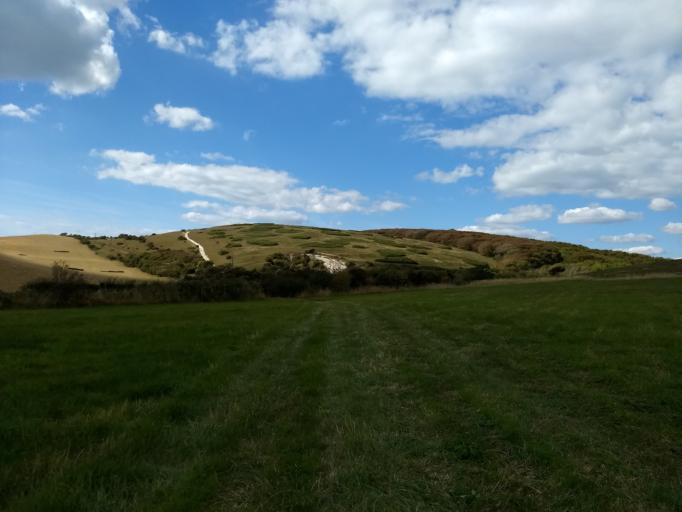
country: GB
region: England
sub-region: Isle of Wight
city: Shalfleet
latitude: 50.6629
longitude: -1.4398
